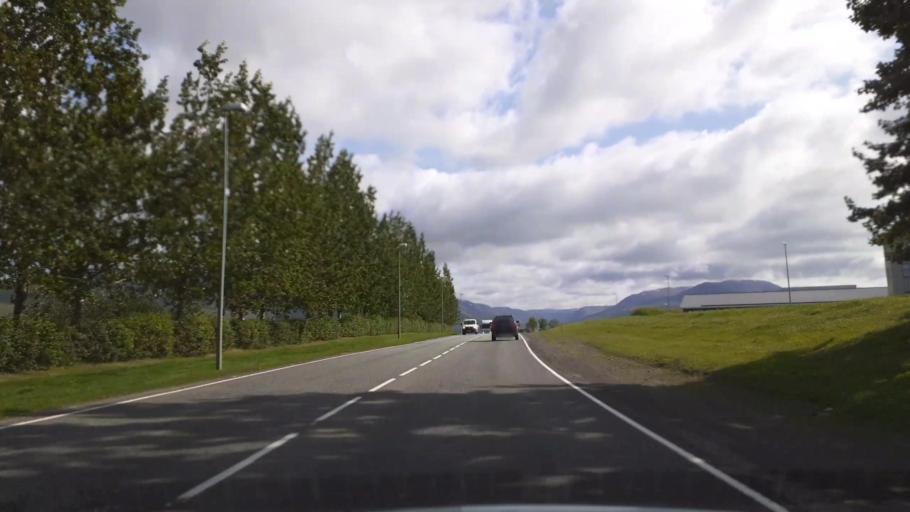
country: IS
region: Northeast
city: Akureyri
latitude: 65.6669
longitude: -18.0936
